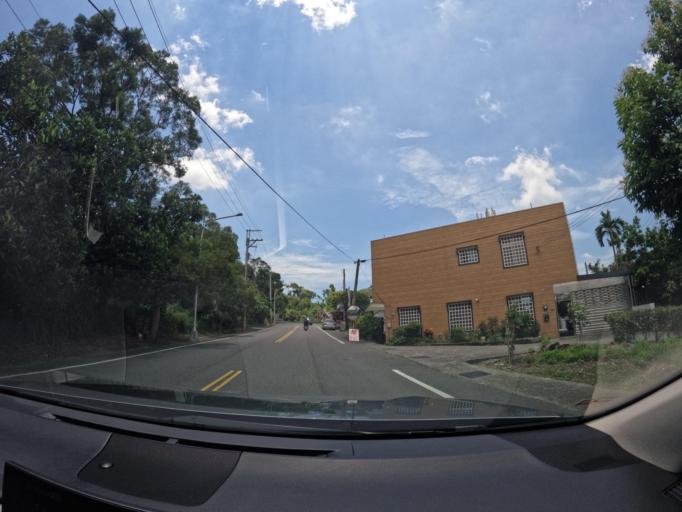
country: TW
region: Taiwan
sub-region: Hsinchu
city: Hsinchu
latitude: 24.6641
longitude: 120.9590
